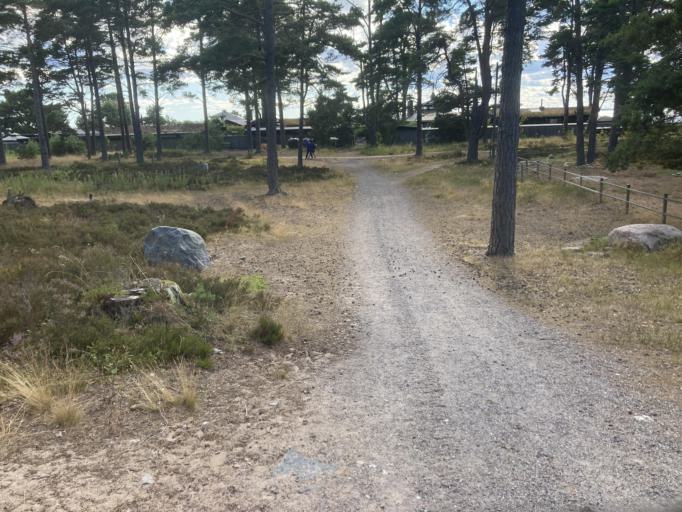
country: SE
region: Stockholm
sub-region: Varmdo Kommun
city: Holo
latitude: 59.2750
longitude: 18.9199
